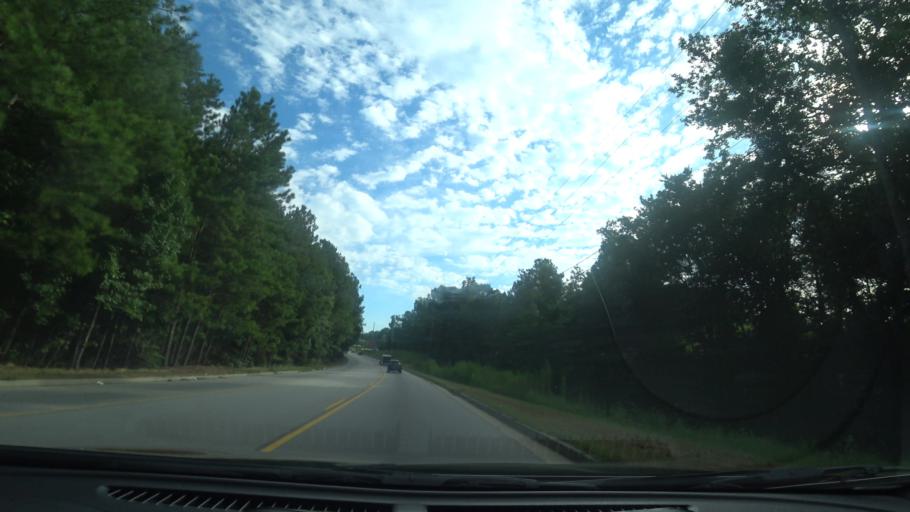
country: US
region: Georgia
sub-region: Rockdale County
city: Conyers
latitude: 33.6446
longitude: -83.9736
